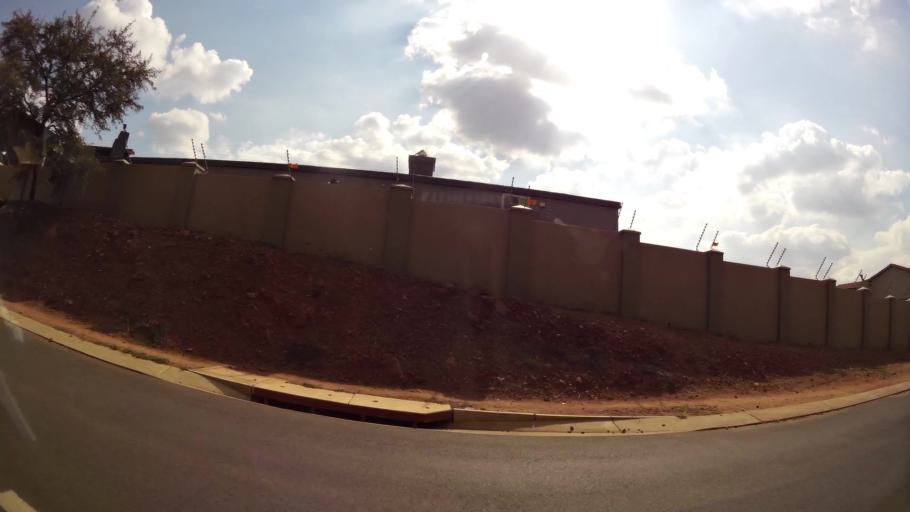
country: ZA
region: Gauteng
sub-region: City of Tshwane Metropolitan Municipality
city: Centurion
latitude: -25.8106
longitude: 28.3452
